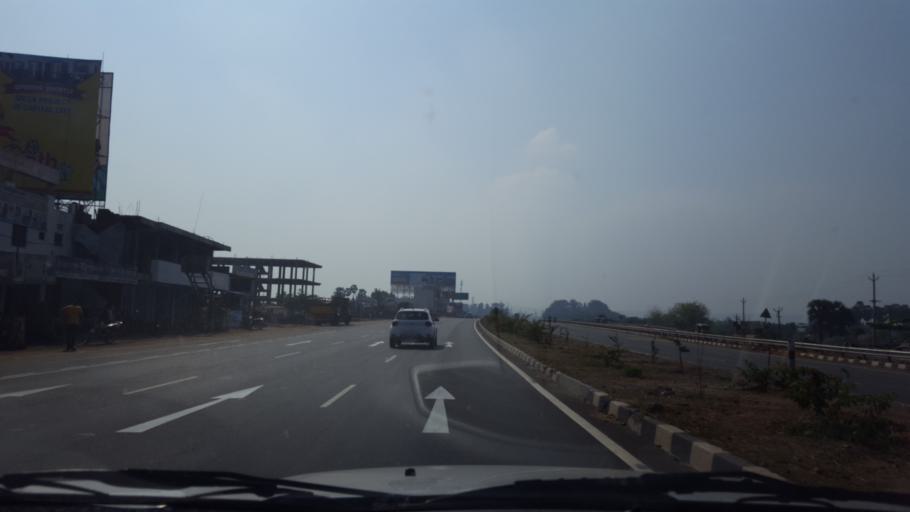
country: IN
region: Andhra Pradesh
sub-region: Vishakhapatnam
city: Bhimunipatnam
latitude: 17.9424
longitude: 83.4205
